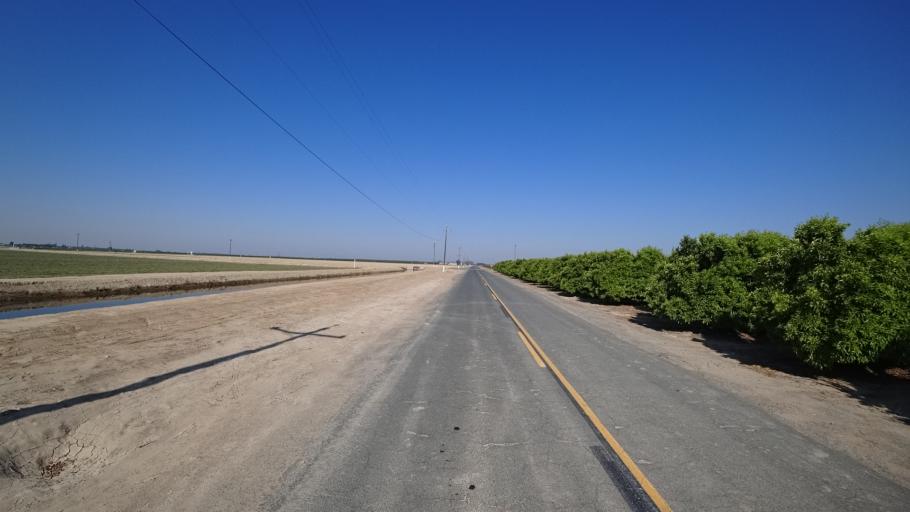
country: US
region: California
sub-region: Kings County
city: Lucerne
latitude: 36.3866
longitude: -119.5634
